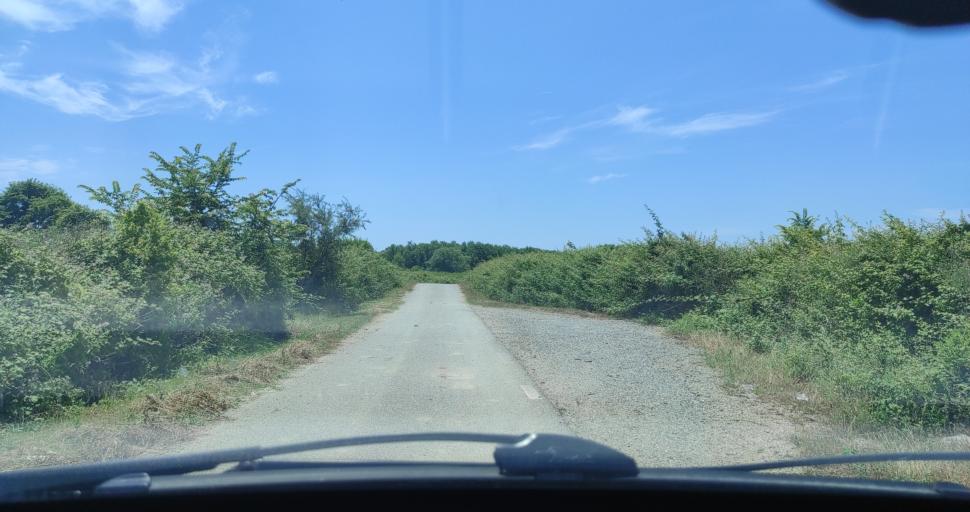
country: AL
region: Shkoder
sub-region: Rrethi i Shkodres
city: Velipoje
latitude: 41.8822
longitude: 19.3842
